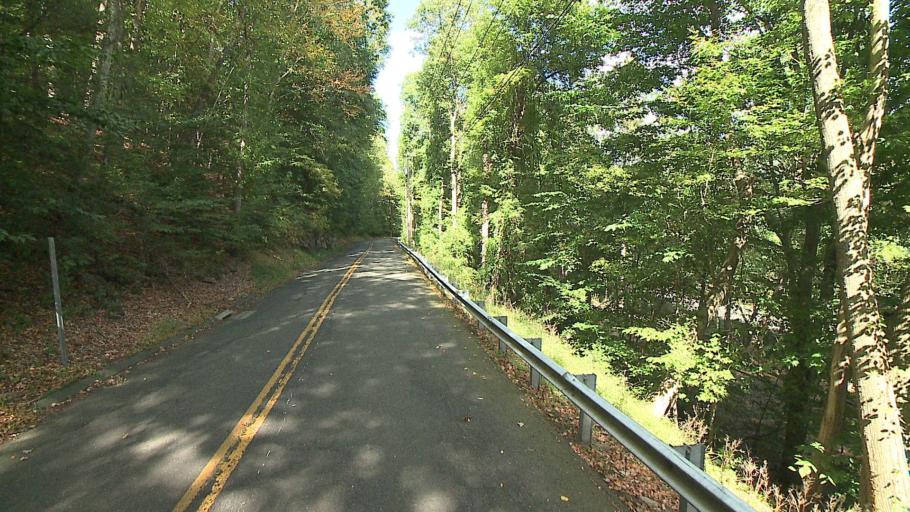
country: US
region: Connecticut
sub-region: Fairfield County
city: Shelton
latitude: 41.3410
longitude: -73.1253
